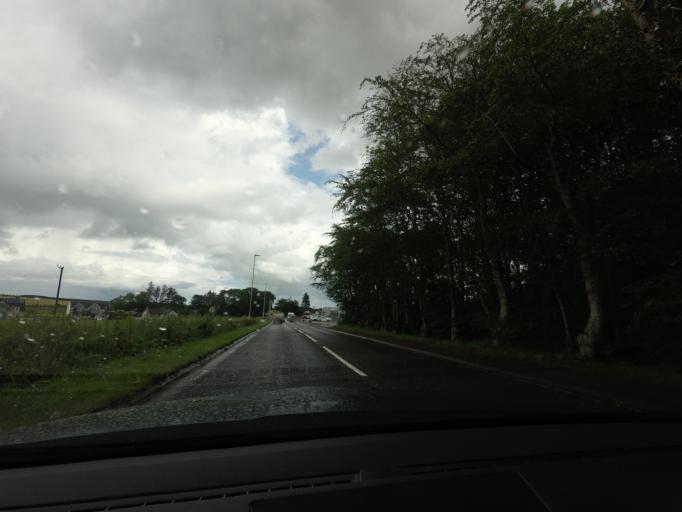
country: GB
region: Scotland
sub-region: Aberdeenshire
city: Turriff
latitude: 57.5436
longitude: -2.4477
